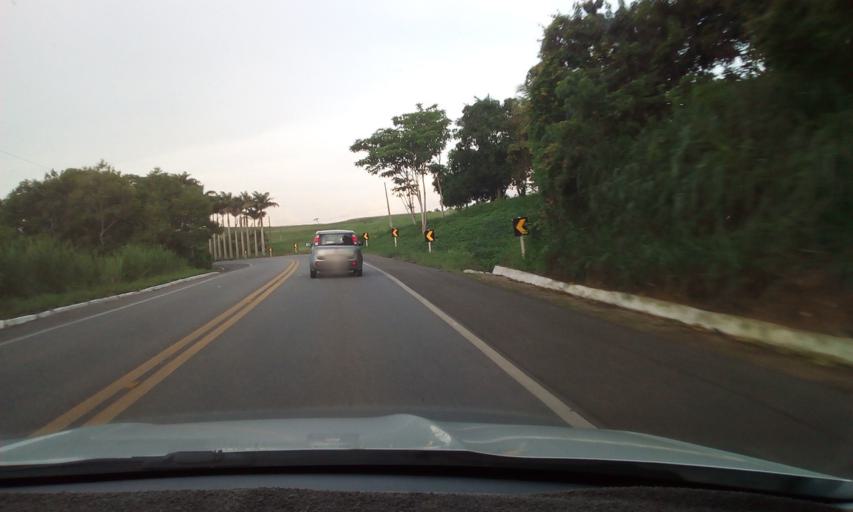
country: BR
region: Pernambuco
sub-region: Vicencia
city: Vicencia
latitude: -7.6293
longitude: -35.2484
